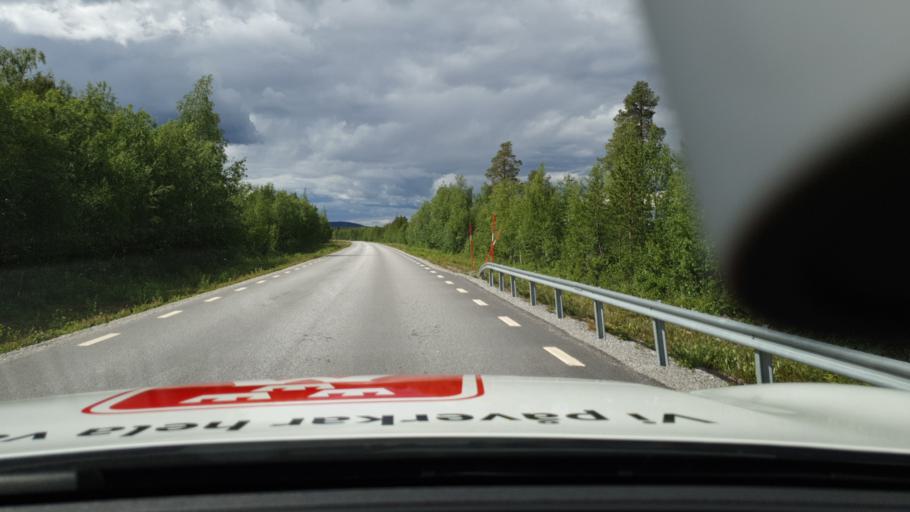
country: SE
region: Norrbotten
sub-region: Jokkmokks Kommun
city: Jokkmokk
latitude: 66.8238
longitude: 19.1995
